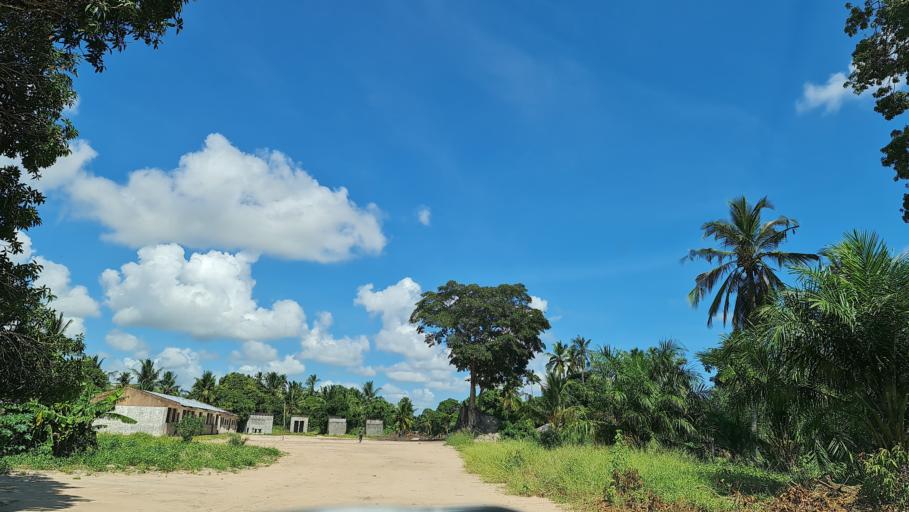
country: MZ
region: Zambezia
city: Quelimane
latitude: -17.3817
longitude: 37.5123
